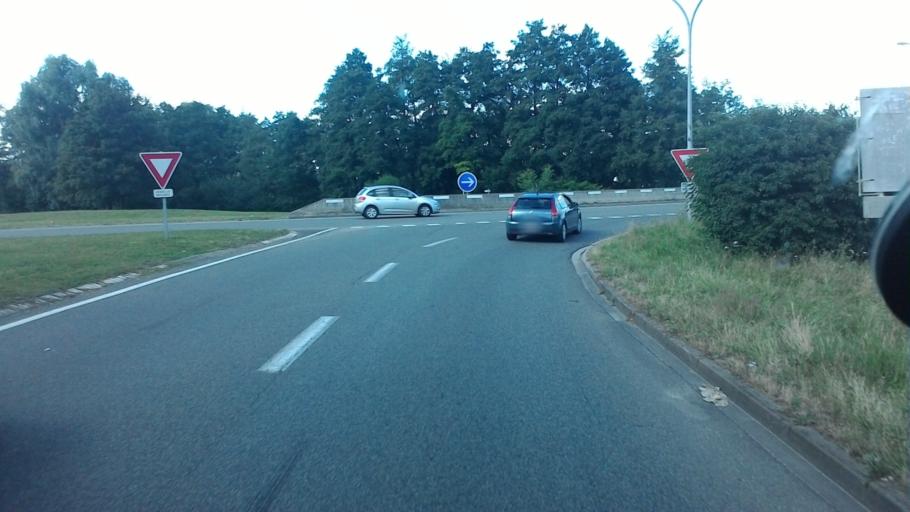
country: FR
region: Franche-Comte
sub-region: Departement de la Haute-Saone
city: Noidans-les-Vesoul
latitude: 47.6253
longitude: 6.1380
